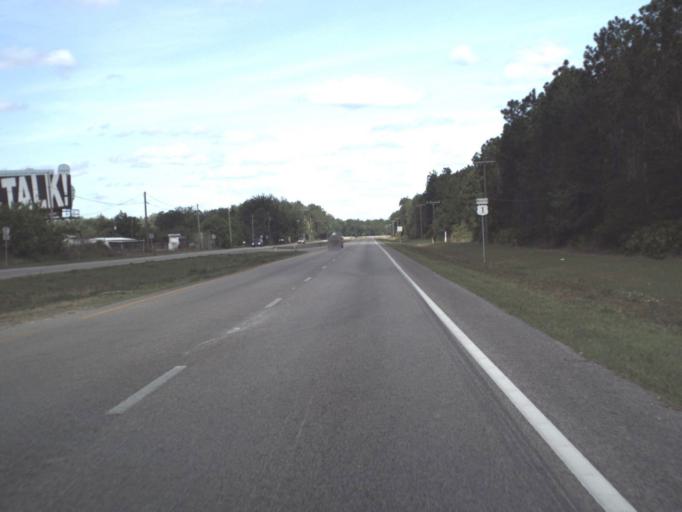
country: US
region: Florida
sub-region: Flagler County
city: Bunnell
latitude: 29.4275
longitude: -81.2232
